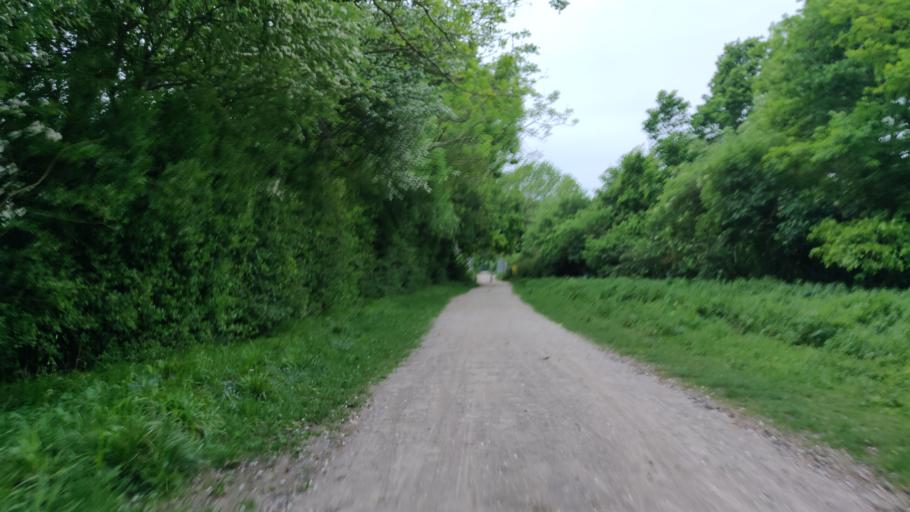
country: GB
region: England
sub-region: West Sussex
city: Partridge Green
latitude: 50.9742
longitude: -0.3159
